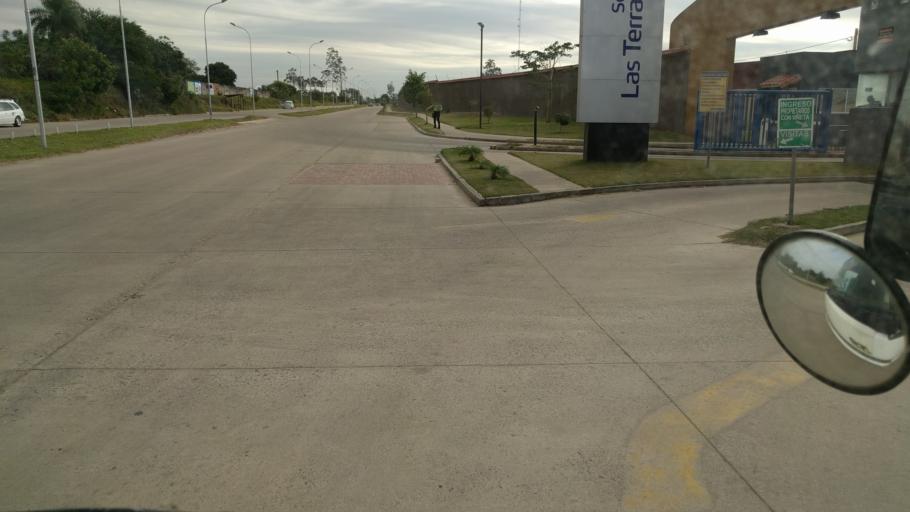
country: BO
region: Santa Cruz
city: Santa Cruz de la Sierra
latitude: -17.6832
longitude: -63.1535
